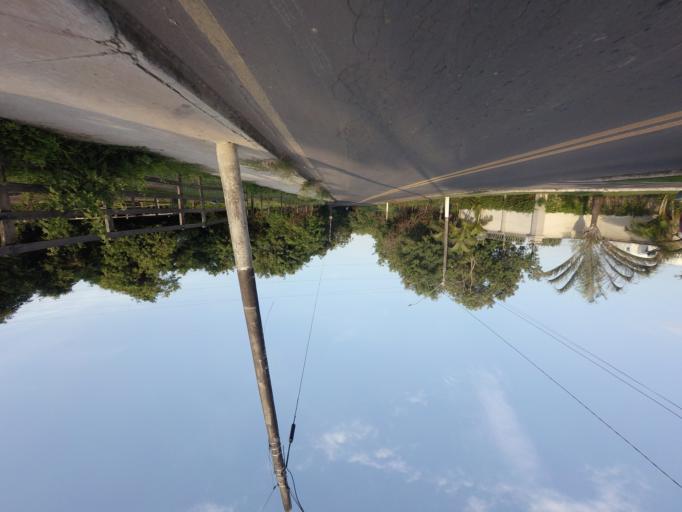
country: BR
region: Sao Paulo
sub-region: Piracicaba
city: Piracicaba
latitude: -22.7543
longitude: -47.6091
